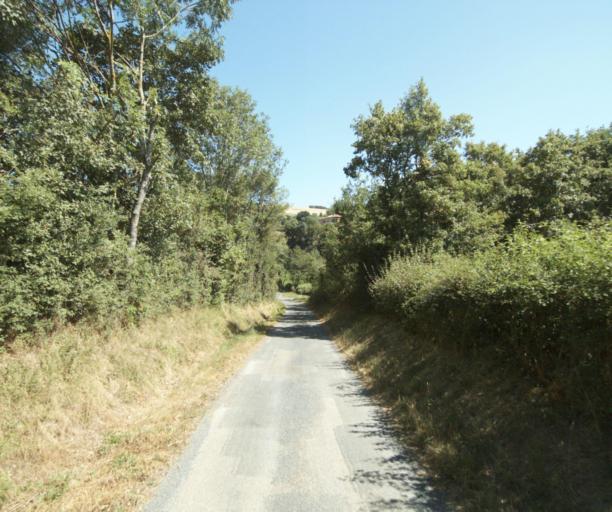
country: FR
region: Rhone-Alpes
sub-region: Departement du Rhone
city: Bessenay
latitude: 45.7933
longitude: 4.5249
